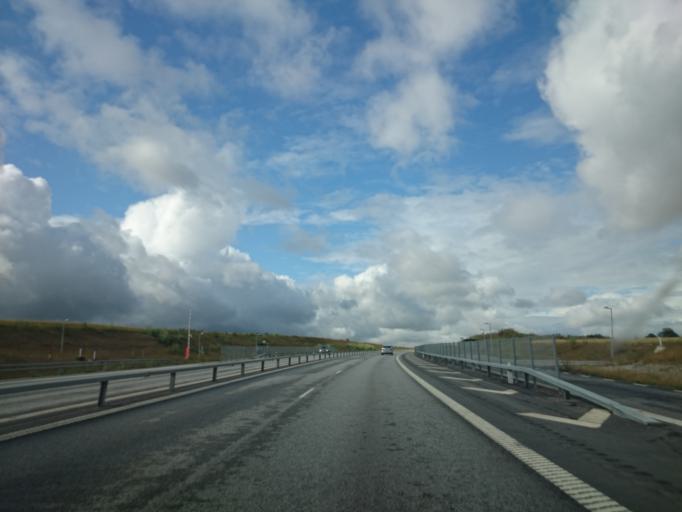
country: SE
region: Skane
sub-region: Hoors Kommun
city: Loberod
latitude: 55.7923
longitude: 13.4430
